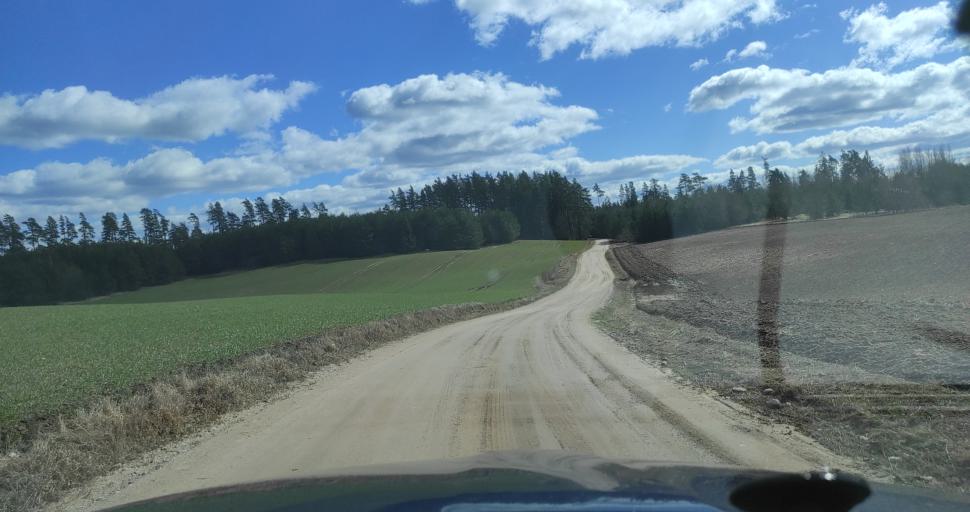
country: LV
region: Kuldigas Rajons
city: Kuldiga
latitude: 56.9564
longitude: 21.9217
